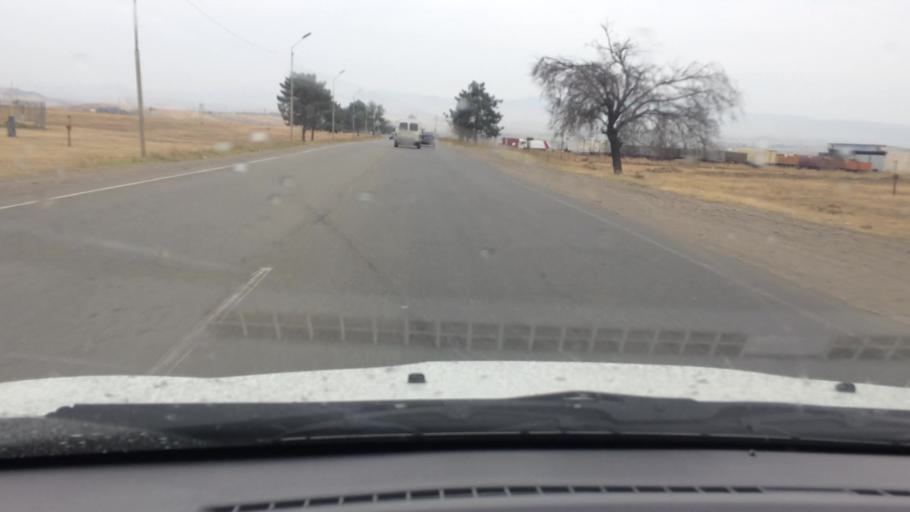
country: GE
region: Kvemo Kartli
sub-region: Marneuli
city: Marneuli
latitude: 41.5114
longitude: 44.7911
